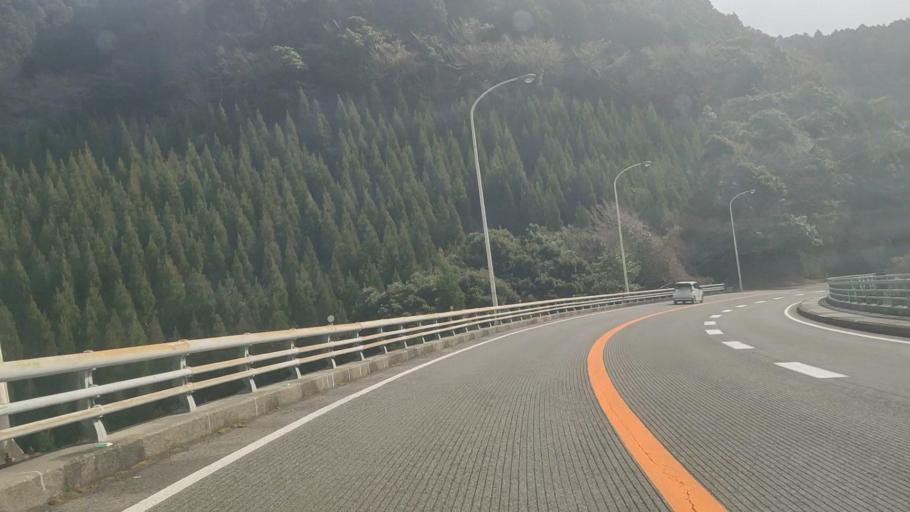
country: JP
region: Kumamoto
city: Hitoyoshi
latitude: 32.0791
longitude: 130.8029
